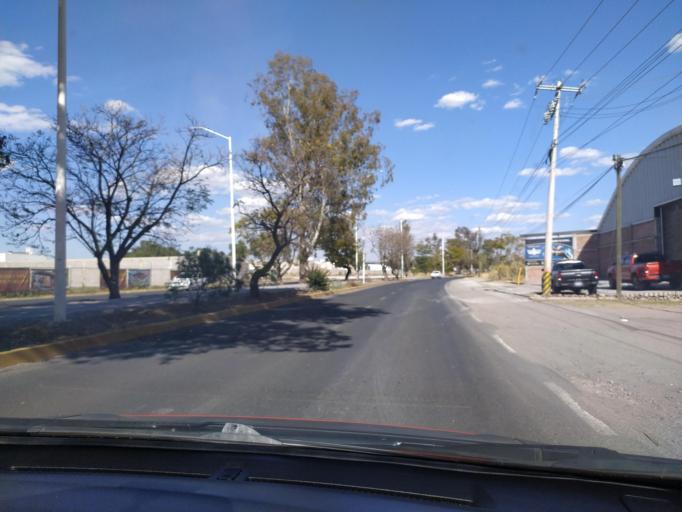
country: LA
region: Oudomxai
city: Muang La
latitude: 21.0311
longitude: 101.8424
